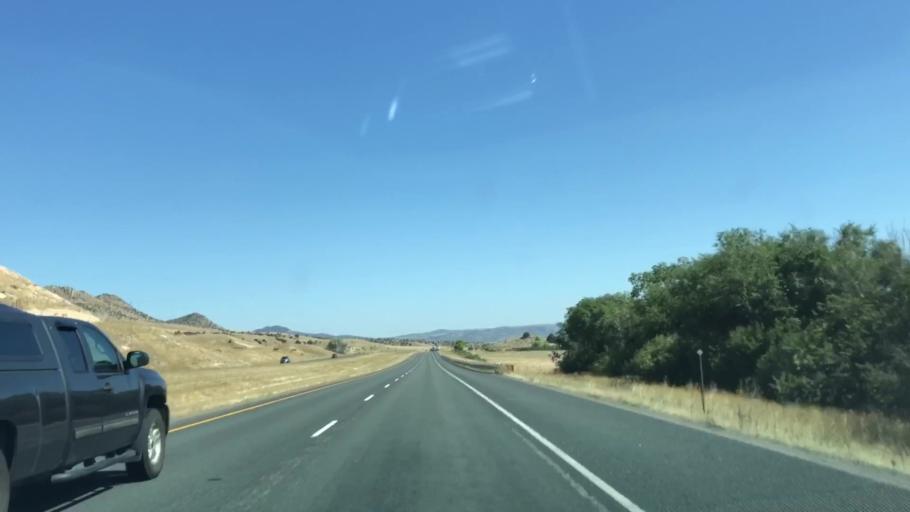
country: US
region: Montana
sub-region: Jefferson County
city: Whitehall
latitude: 45.8756
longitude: -112.0675
